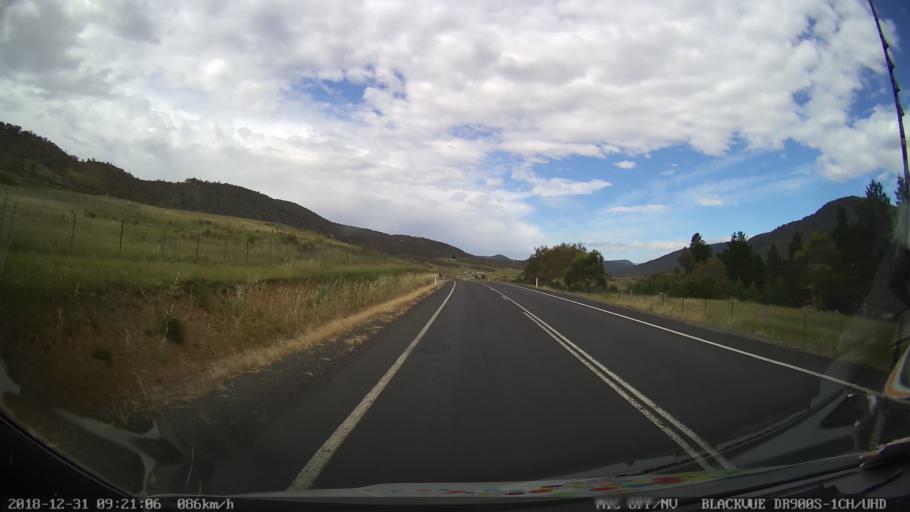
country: AU
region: New South Wales
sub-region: Snowy River
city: Jindabyne
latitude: -36.4264
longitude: 148.5659
